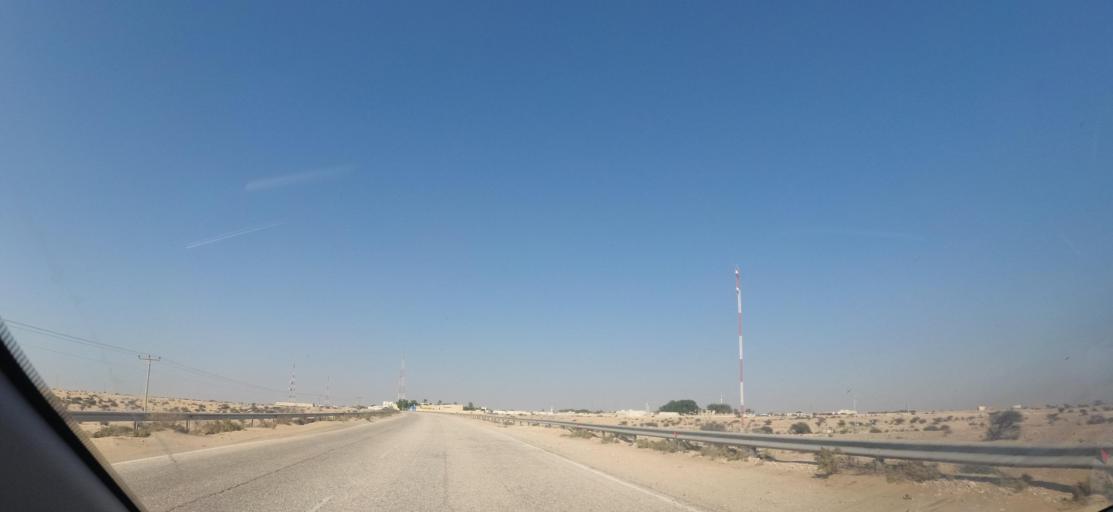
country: QA
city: Al Jumayliyah
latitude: 25.6126
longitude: 51.0785
